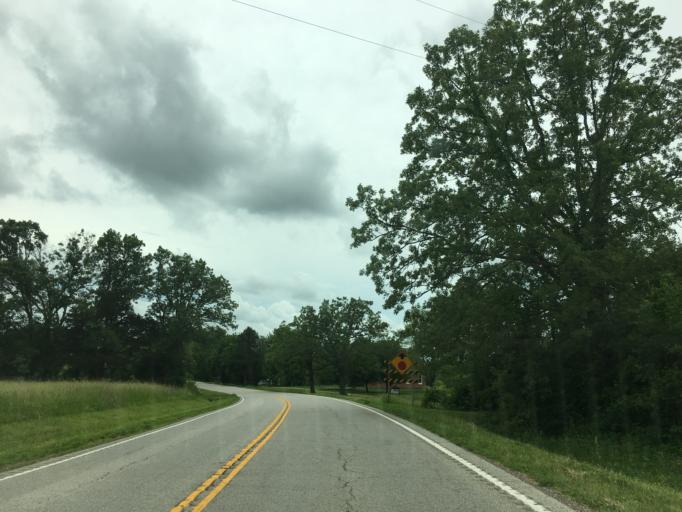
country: US
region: Missouri
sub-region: Gasconade County
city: Owensville
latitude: 38.4737
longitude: -91.4642
